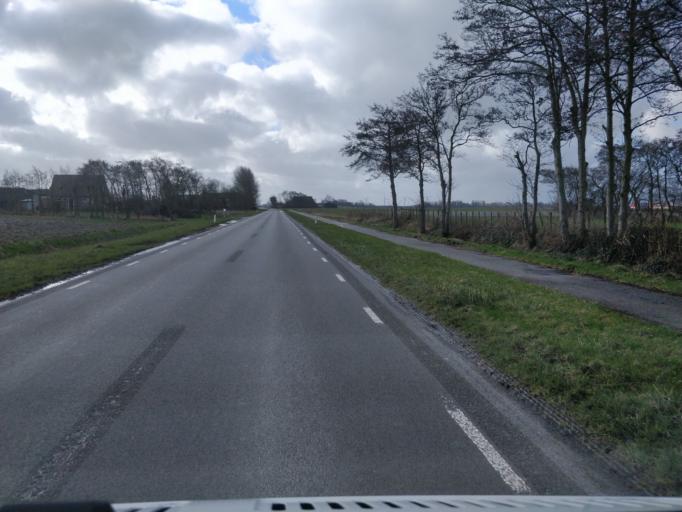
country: NL
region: Friesland
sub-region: Gemeente Franekeradeel
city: Sexbierum
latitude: 53.2113
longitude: 5.4675
